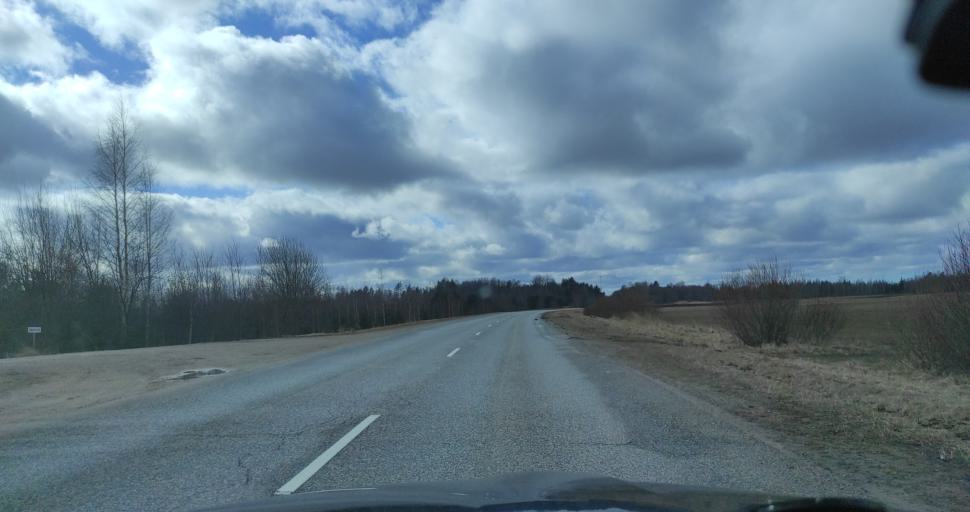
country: LV
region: Kuldigas Rajons
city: Kuldiga
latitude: 56.9852
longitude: 22.0697
